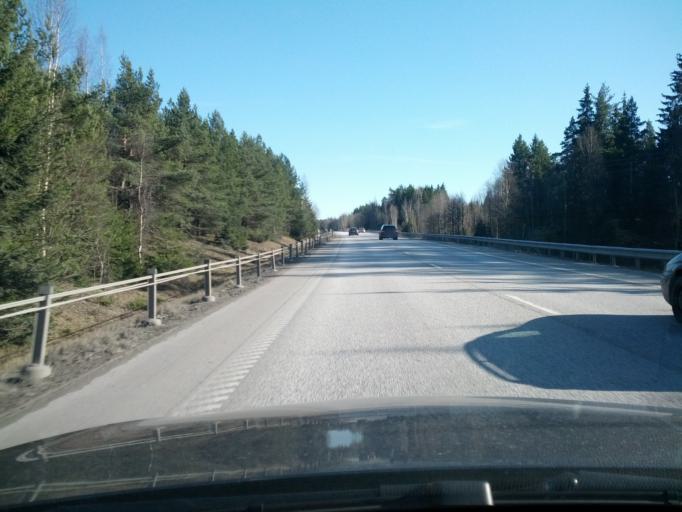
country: SE
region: Stockholm
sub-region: Upplands-Bro Kommun
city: Bro
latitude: 59.5494
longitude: 17.5948
